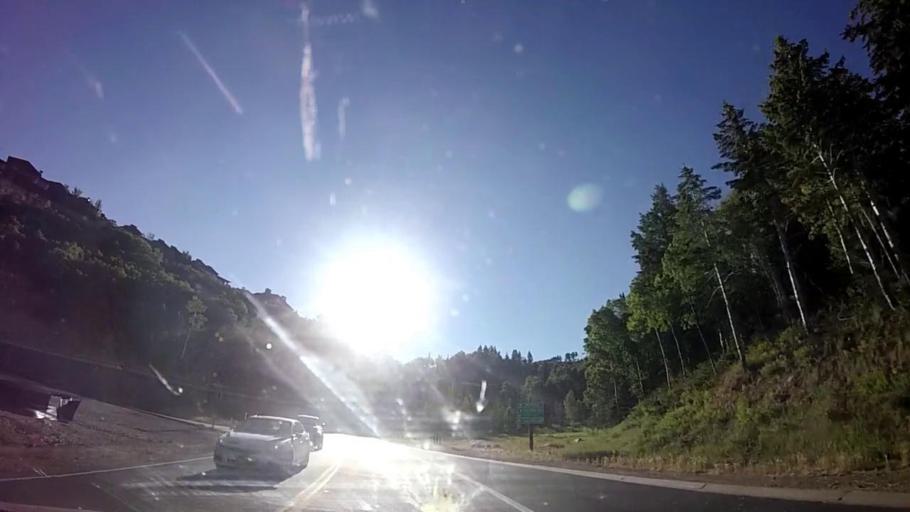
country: US
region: Utah
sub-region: Summit County
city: Park City
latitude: 40.6204
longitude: -111.4928
